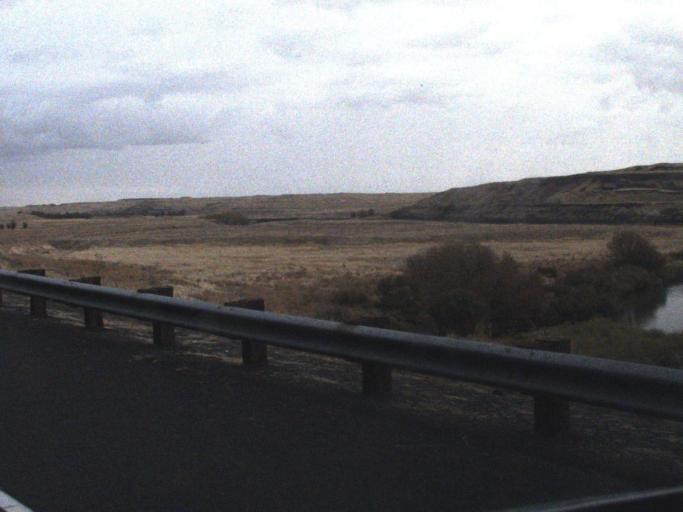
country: US
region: Washington
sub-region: Adams County
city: Ritzville
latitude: 46.7521
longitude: -118.1910
